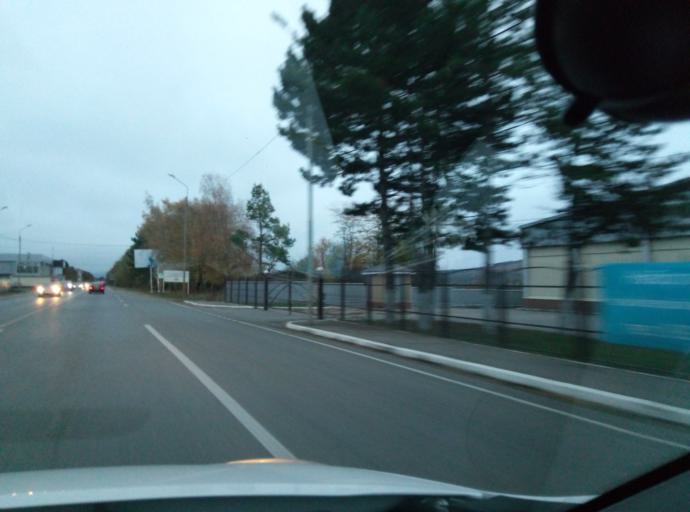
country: RU
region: Stavropol'skiy
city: Yessentukskaya
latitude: 44.0546
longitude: 42.9217
